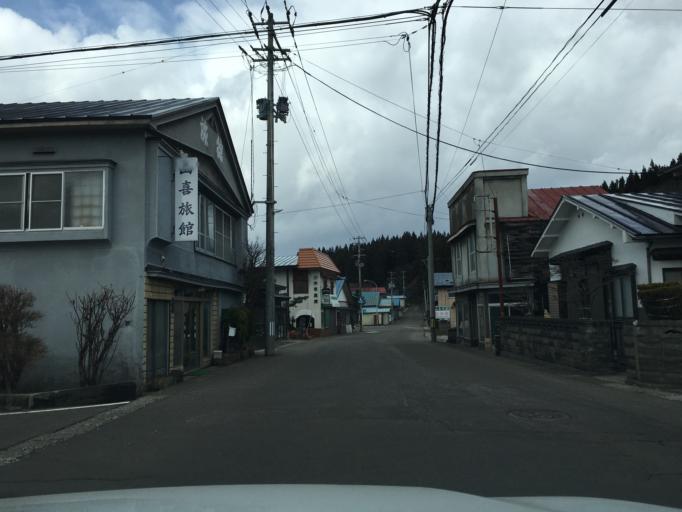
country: JP
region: Akita
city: Takanosu
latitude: 40.1616
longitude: 140.3290
